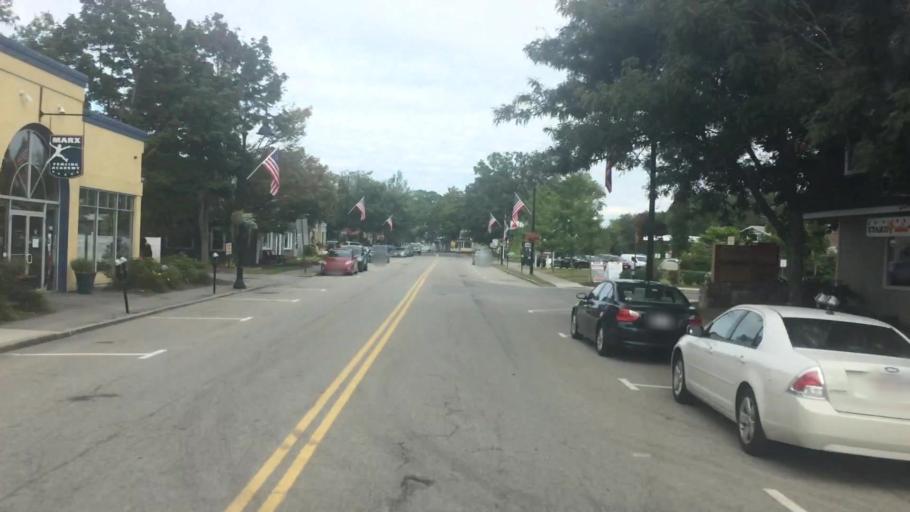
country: US
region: Massachusetts
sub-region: Middlesex County
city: West Concord
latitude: 42.4575
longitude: -71.3959
